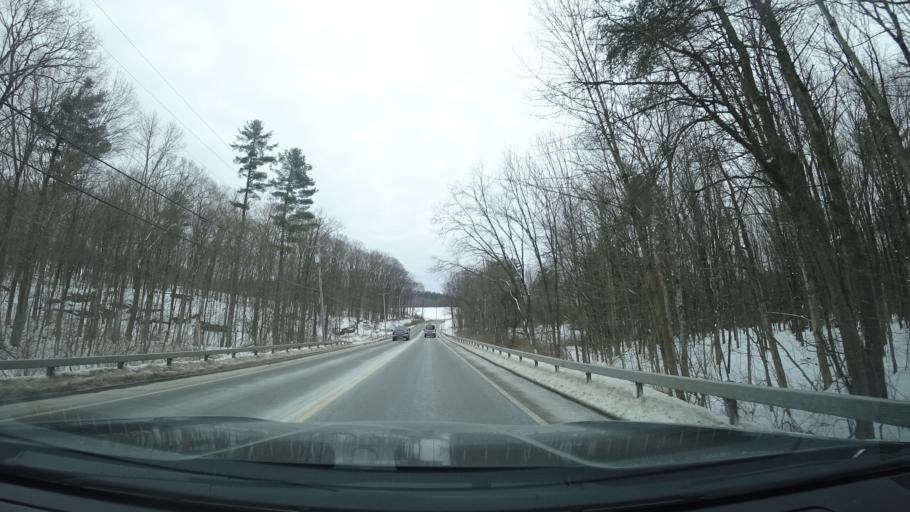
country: US
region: New York
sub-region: Washington County
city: Fort Edward
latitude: 43.2087
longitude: -73.4871
